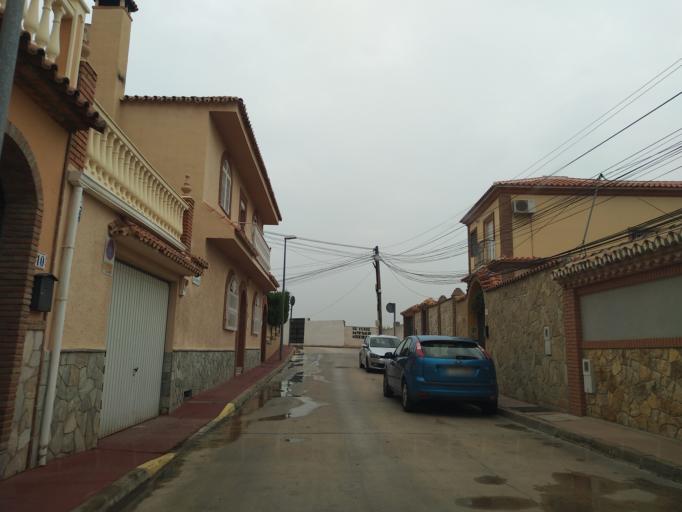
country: ES
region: Andalusia
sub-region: Provincia de Malaga
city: Malaga
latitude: 36.7444
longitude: -4.4771
